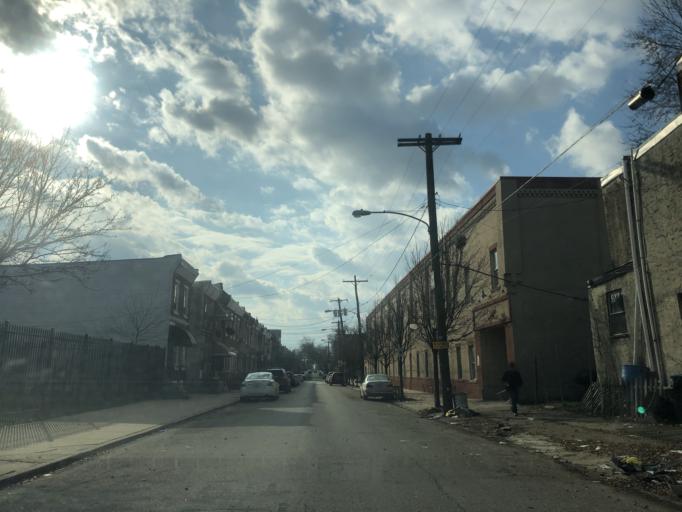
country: US
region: Pennsylvania
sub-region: Philadelphia County
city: Philadelphia
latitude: 39.9379
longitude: -75.1968
